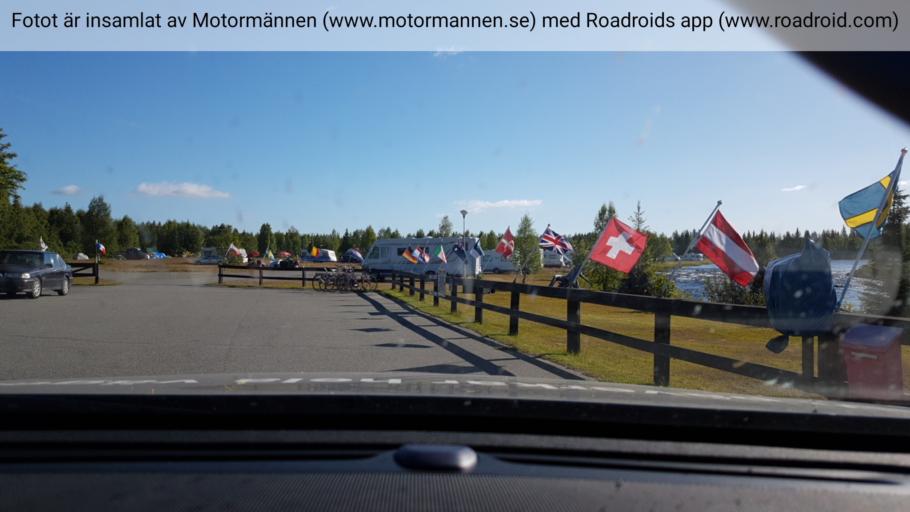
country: SE
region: Vaesterbotten
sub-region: Vilhelmina Kommun
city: Vilhelmina
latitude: 64.7928
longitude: 16.7978
